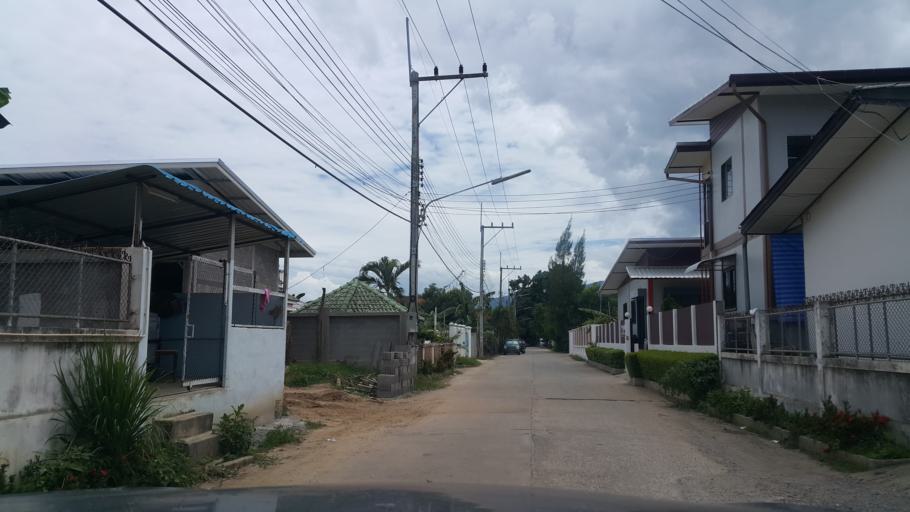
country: TH
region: Chiang Mai
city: San Sai
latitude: 18.8414
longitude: 99.0215
